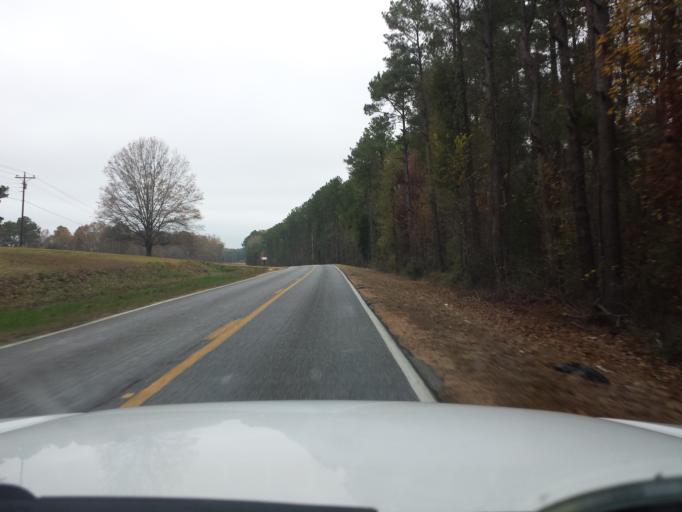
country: US
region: Mississippi
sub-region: Madison County
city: Canton
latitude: 32.4804
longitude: -89.9165
